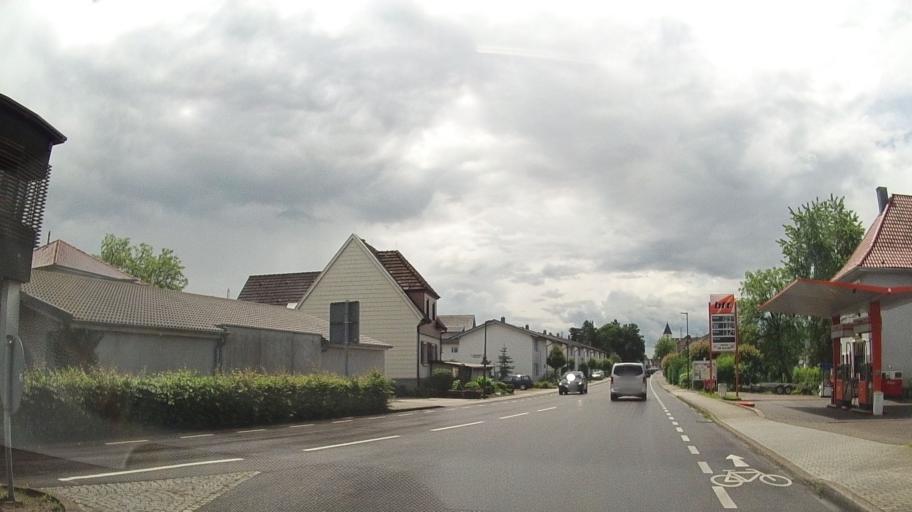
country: DE
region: Baden-Wuerttemberg
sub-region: Freiburg Region
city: Renchen
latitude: 48.5906
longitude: 8.0166
